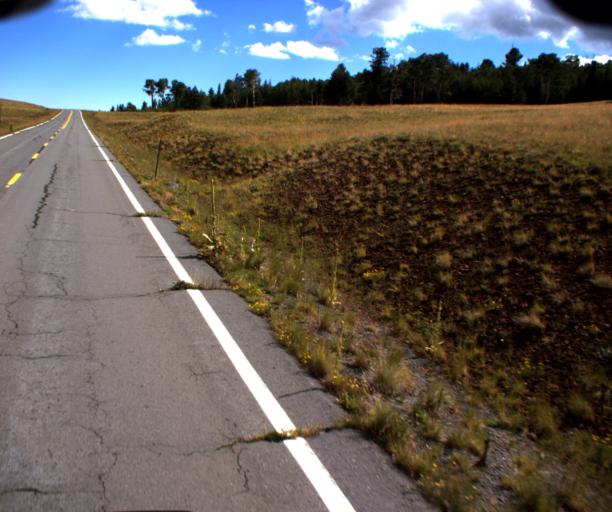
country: US
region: Arizona
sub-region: Apache County
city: Eagar
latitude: 33.9818
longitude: -109.3714
